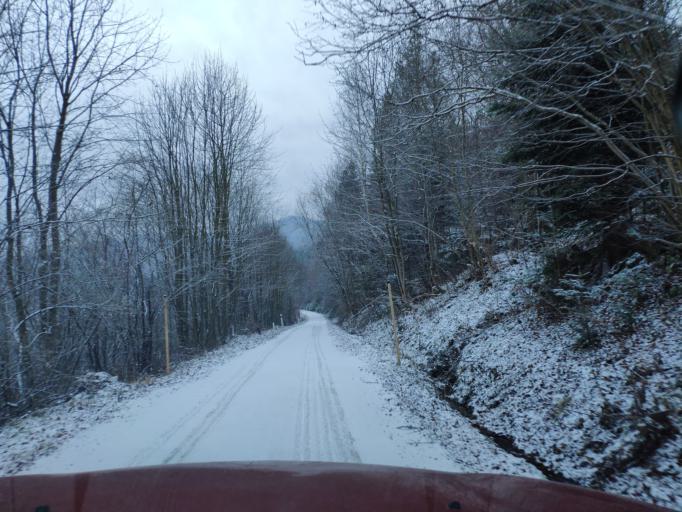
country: SK
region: Kosicky
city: Spisska Nova Ves
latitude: 48.8132
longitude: 20.5558
